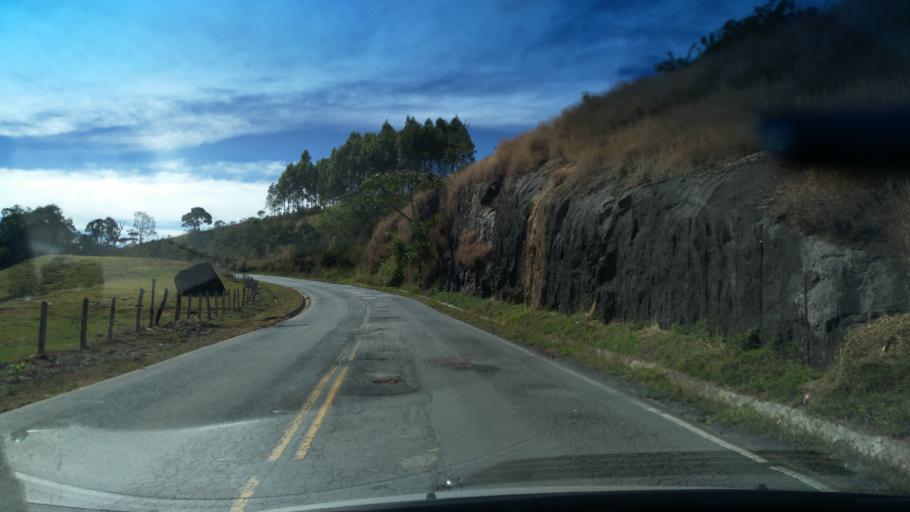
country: BR
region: Minas Gerais
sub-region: Andradas
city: Andradas
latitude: -22.0525
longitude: -46.3616
